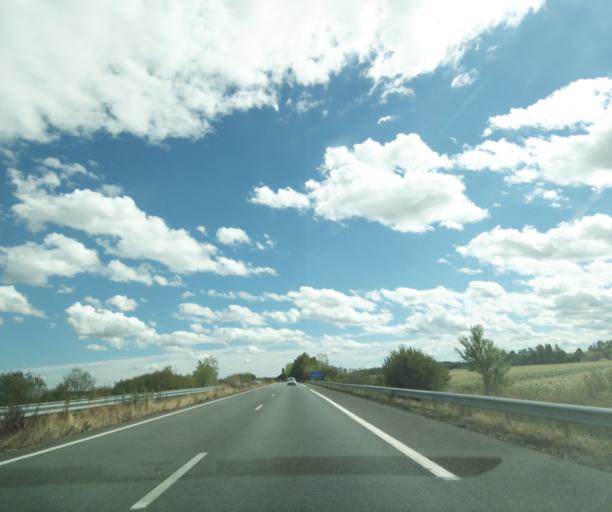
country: FR
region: Aquitaine
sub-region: Departement du Lot-et-Garonne
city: Meilhan-sur-Garonne
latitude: 44.4853
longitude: 0.0090
